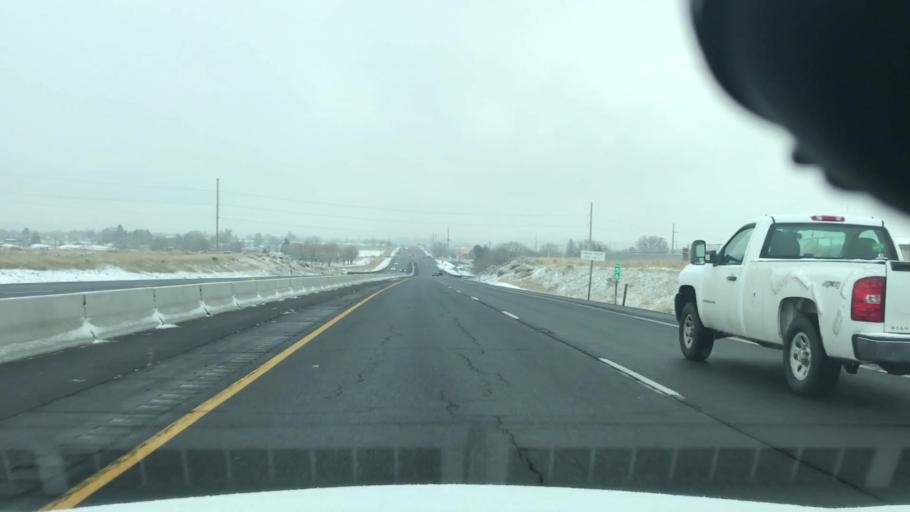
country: US
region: Washington
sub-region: Grant County
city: Cascade Valley
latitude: 47.1527
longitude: -119.3020
